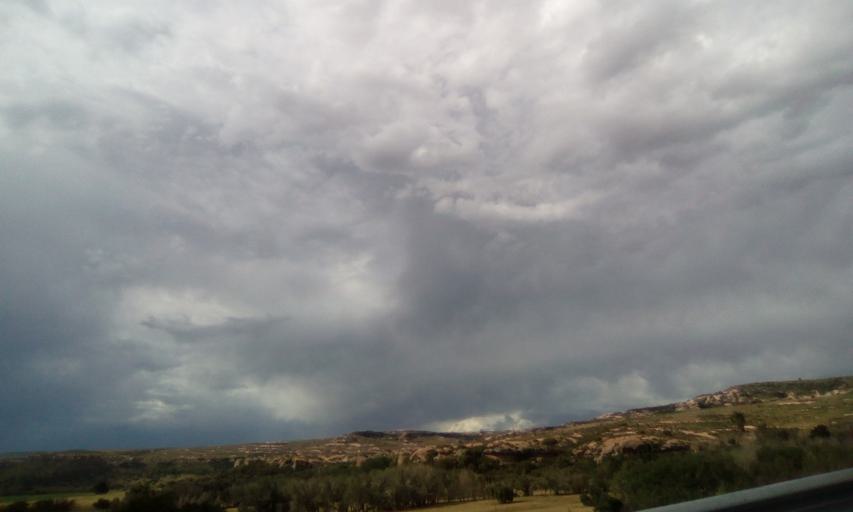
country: ZA
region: Orange Free State
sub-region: Thabo Mofutsanyana District Municipality
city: Ladybrand
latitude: -29.2498
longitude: 27.4346
